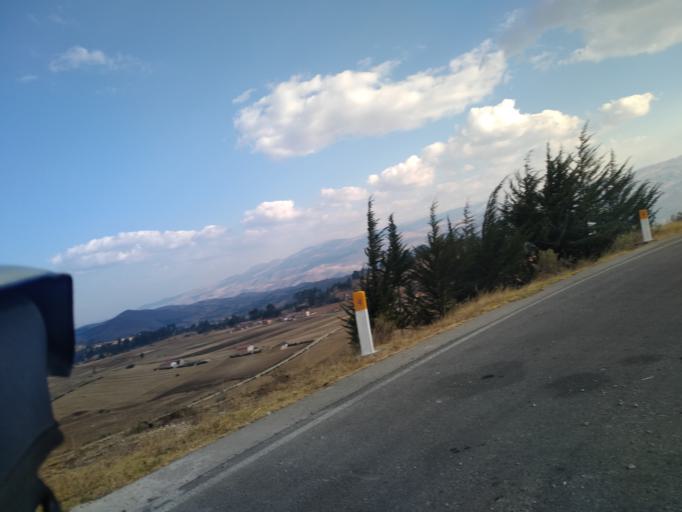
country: PE
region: Cajamarca
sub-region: Provincia de Cajamarca
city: Llacanora
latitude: -7.1540
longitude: -78.4143
